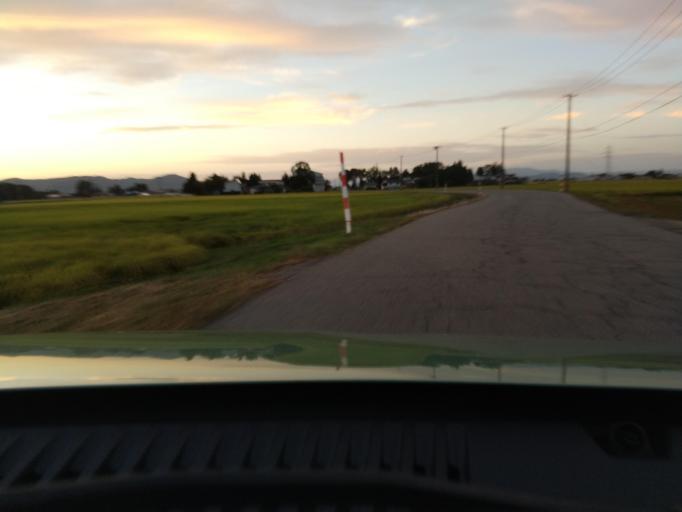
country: JP
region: Akita
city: Omagari
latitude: 39.3997
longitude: 140.5058
